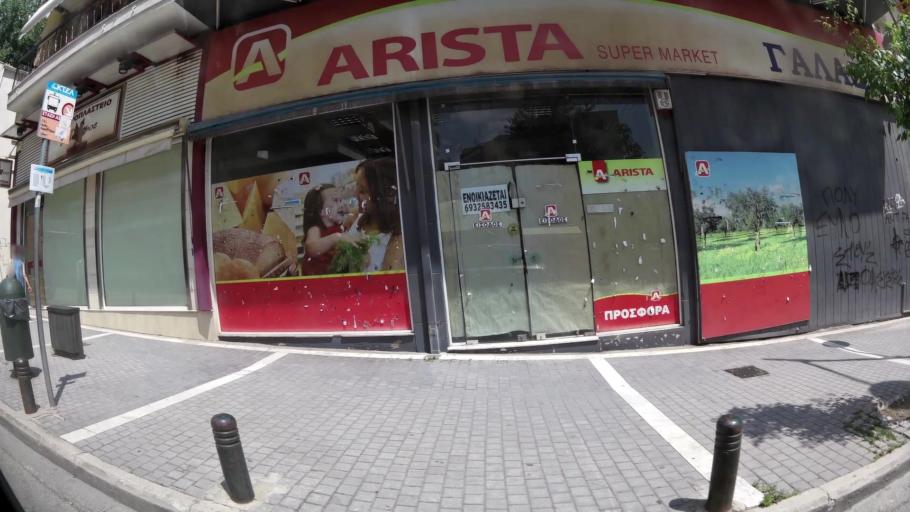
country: GR
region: West Macedonia
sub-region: Nomos Kozanis
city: Kozani
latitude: 40.3039
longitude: 21.7888
